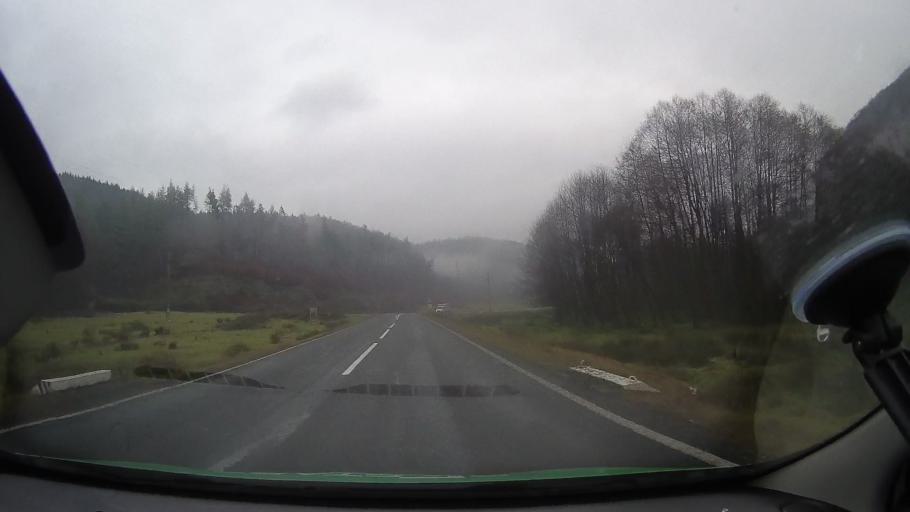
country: RO
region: Arad
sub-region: Comuna Plescuta
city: Plescuta
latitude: 46.3175
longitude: 22.4591
